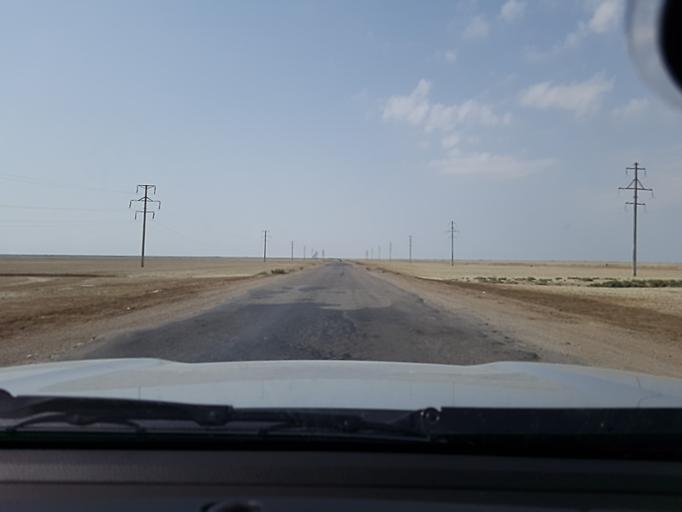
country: TM
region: Balkan
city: Gumdag
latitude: 39.0636
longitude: 54.5841
